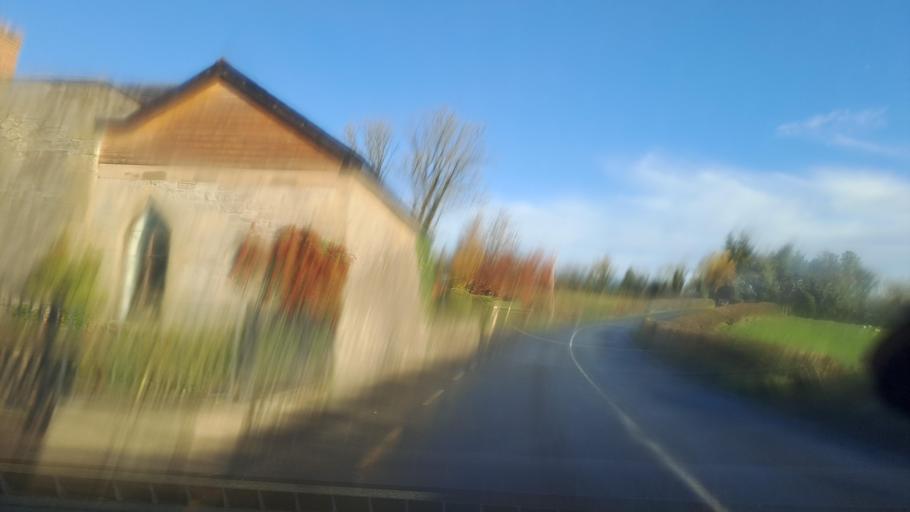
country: IE
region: Ulster
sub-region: County Monaghan
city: Monaghan
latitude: 54.1534
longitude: -7.0040
